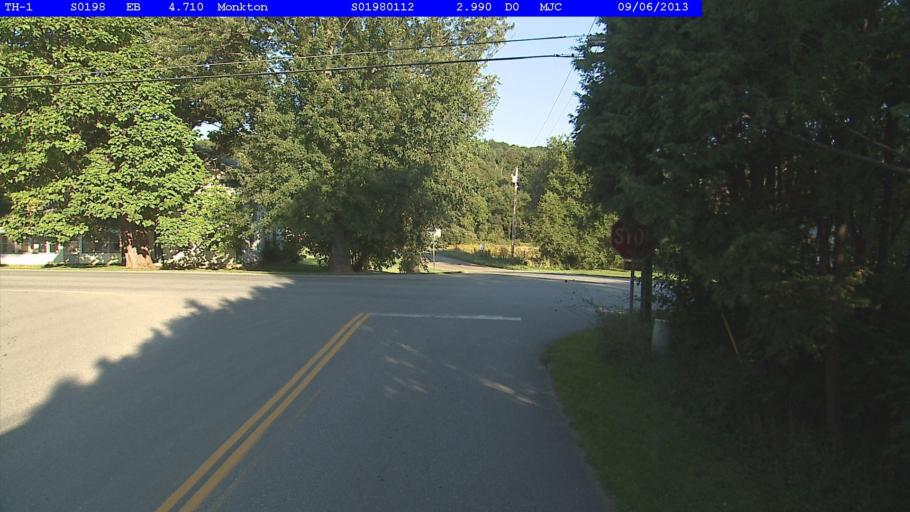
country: US
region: Vermont
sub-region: Chittenden County
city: Hinesburg
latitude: 44.2369
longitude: -73.1451
